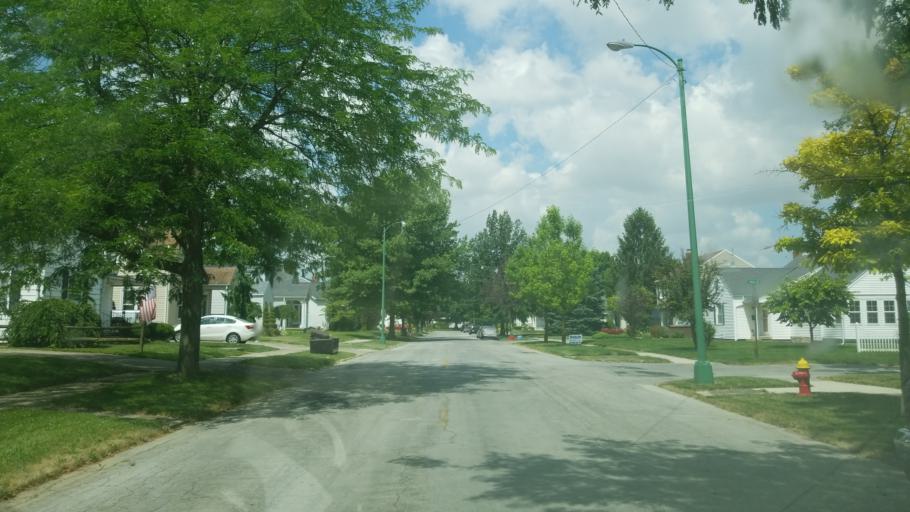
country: US
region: Ohio
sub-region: Auglaize County
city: Wapakoneta
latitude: 40.5671
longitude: -84.2051
